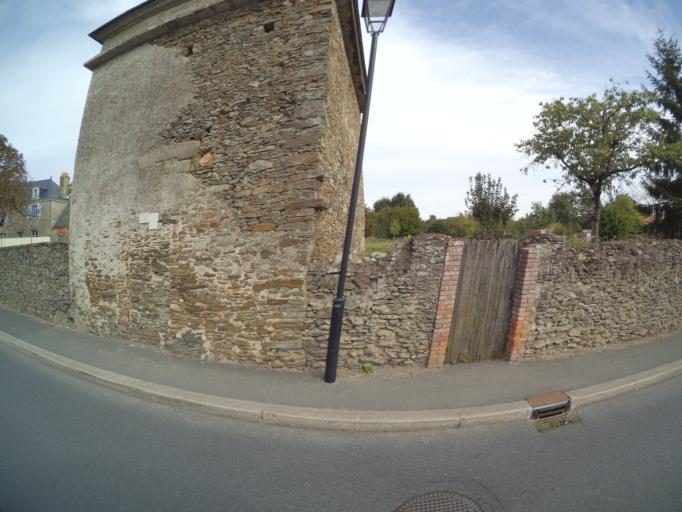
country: FR
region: Pays de la Loire
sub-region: Departement de Maine-et-Loire
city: Saint-Lambert-du-Lattay
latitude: 47.2173
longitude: -0.6092
